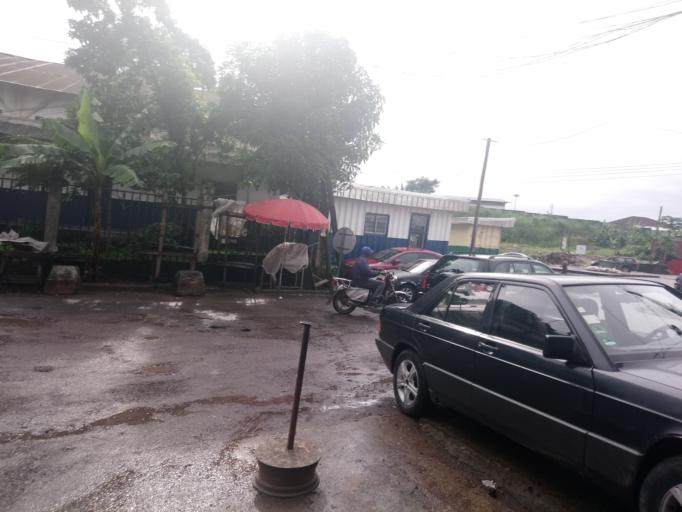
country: CM
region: Littoral
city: Douala
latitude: 4.0331
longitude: 9.6828
